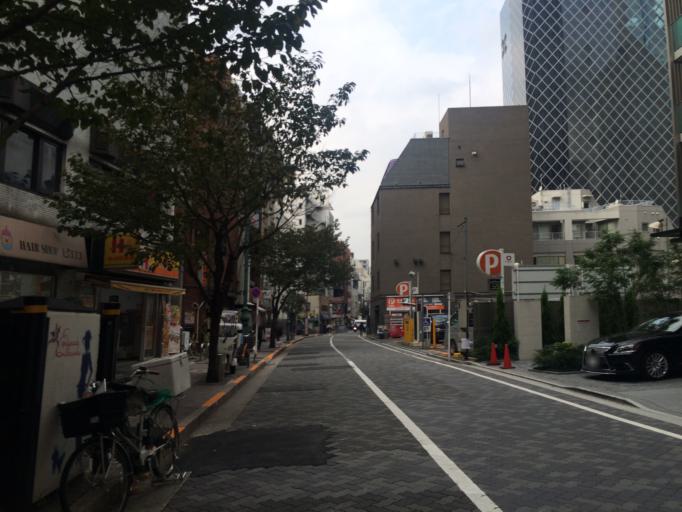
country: JP
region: Tokyo
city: Tokyo
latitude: 35.6721
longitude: 139.7390
